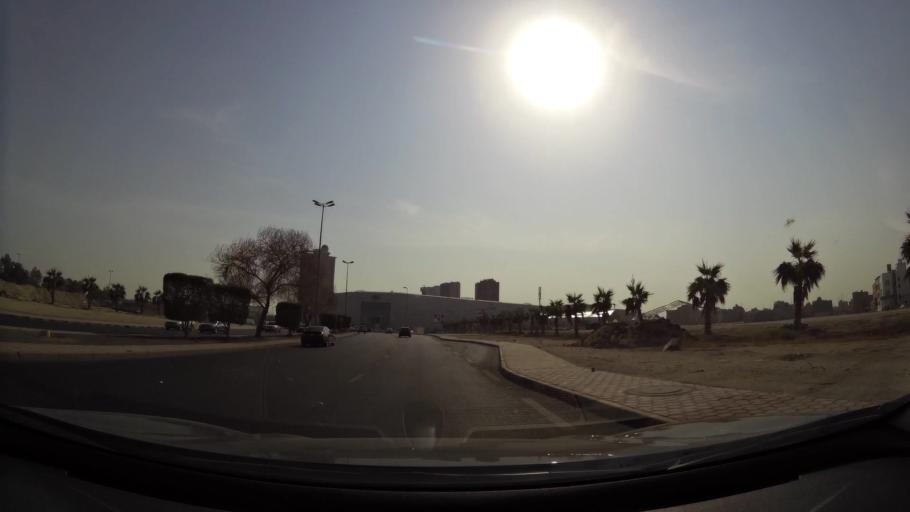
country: KW
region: Mubarak al Kabir
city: Mubarak al Kabir
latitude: 29.1779
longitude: 48.1004
